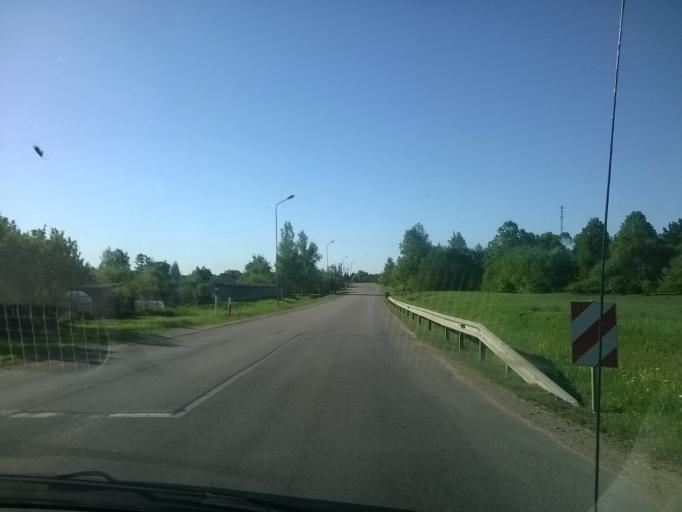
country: LV
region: Valkas Rajons
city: Valka
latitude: 57.7702
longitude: 25.9997
